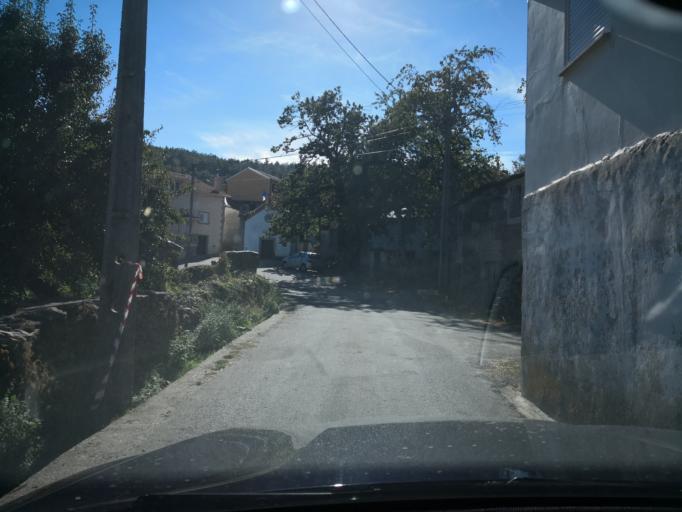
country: PT
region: Vila Real
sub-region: Santa Marta de Penaguiao
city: Santa Marta de Penaguiao
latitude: 41.2832
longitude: -7.8694
